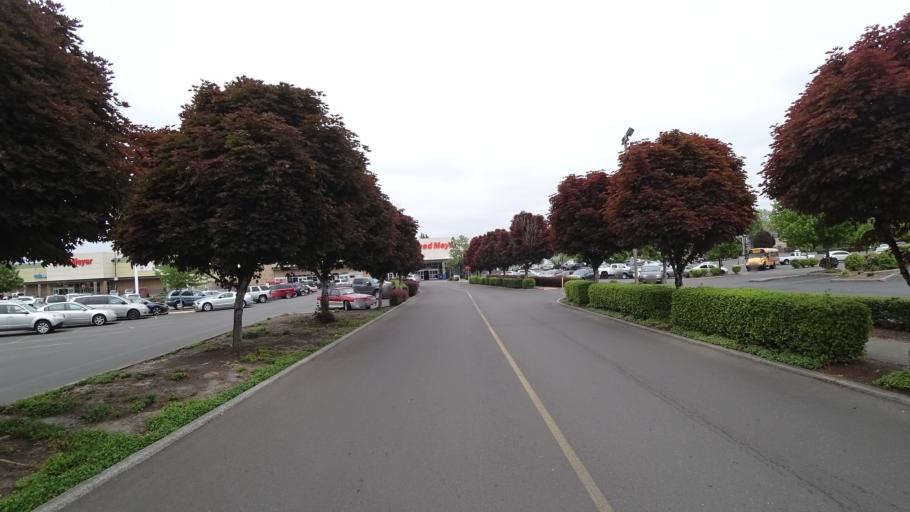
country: US
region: Oregon
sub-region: Washington County
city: Aloha
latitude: 45.4990
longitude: -122.9137
